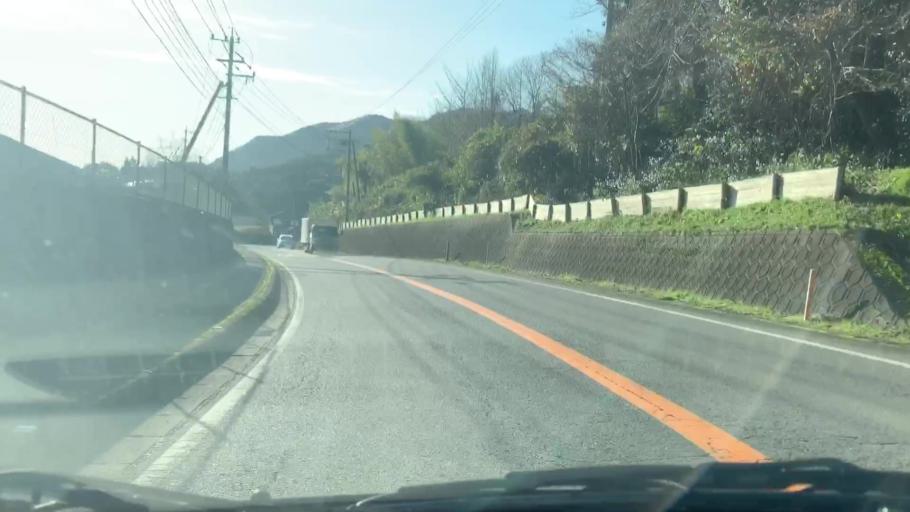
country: JP
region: Saga Prefecture
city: Takeocho-takeo
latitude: 33.2361
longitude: 130.0122
